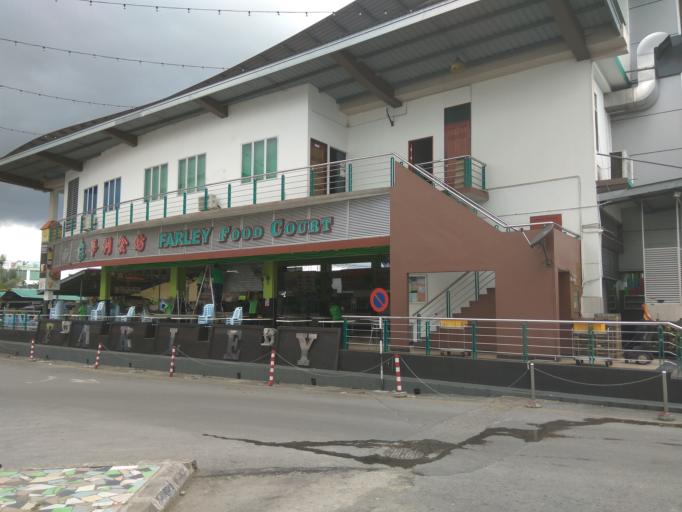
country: MY
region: Sarawak
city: Sibu
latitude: 2.2666
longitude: 111.8633
